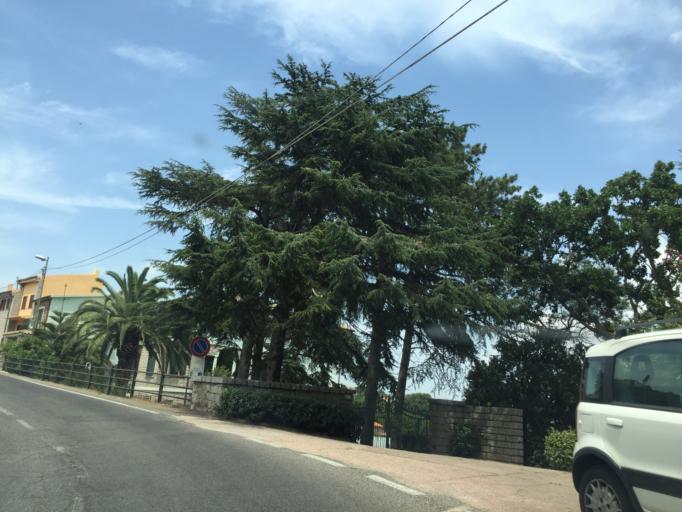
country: IT
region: Sardinia
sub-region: Provincia di Olbia-Tempio
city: Aggius
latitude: 40.9258
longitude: 9.0644
